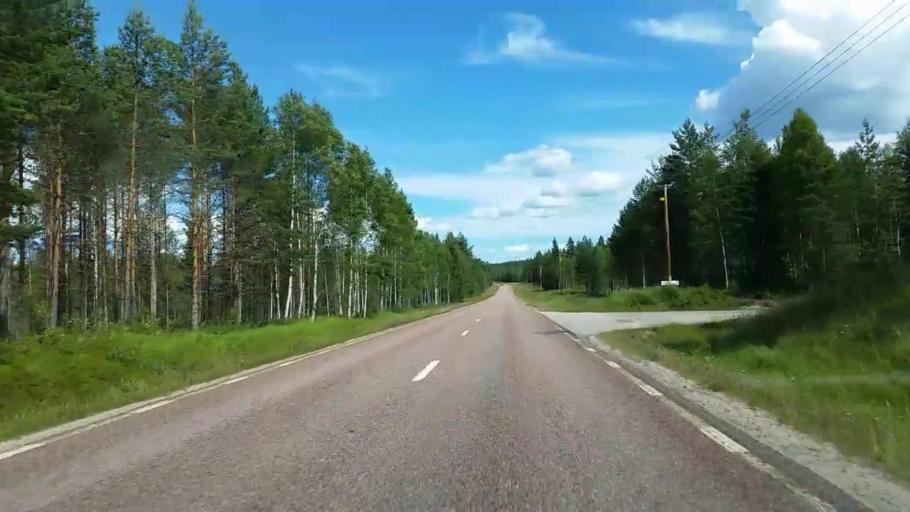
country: SE
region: Dalarna
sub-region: Rattviks Kommun
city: Raettvik
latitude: 61.1950
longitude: 15.3316
